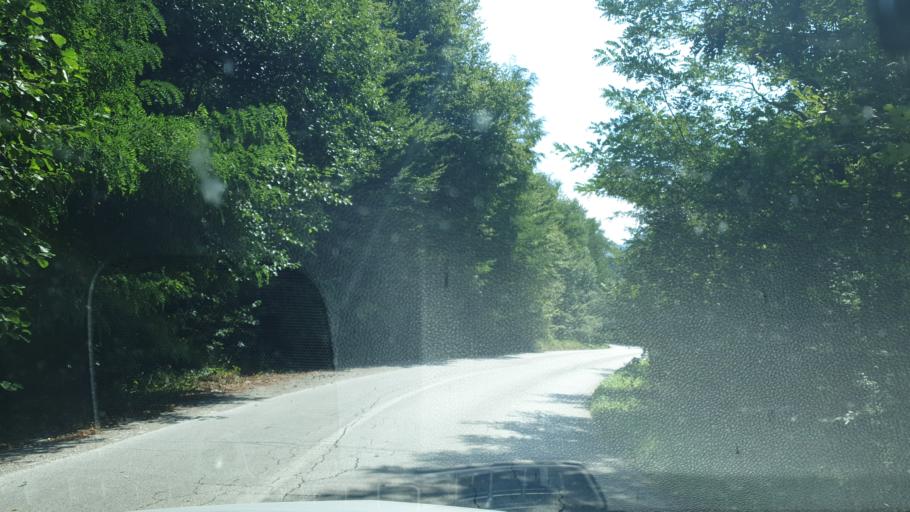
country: RS
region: Central Serbia
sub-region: Zlatiborski Okrug
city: Cajetina
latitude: 43.6728
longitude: 19.8269
